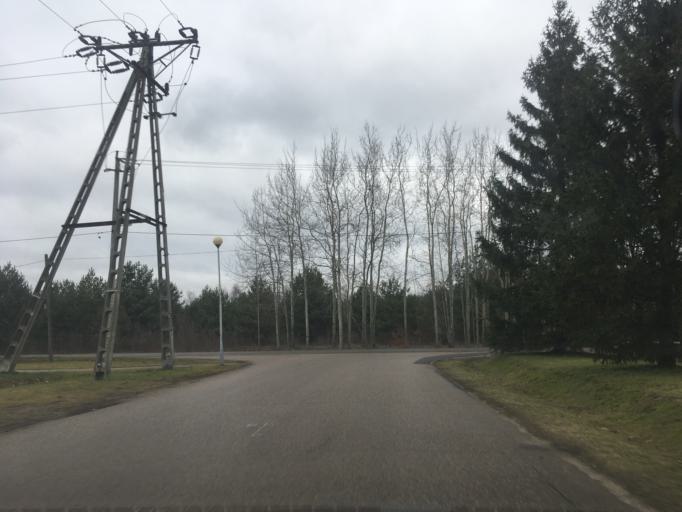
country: PL
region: Masovian Voivodeship
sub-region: Powiat piaseczynski
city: Lesznowola
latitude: 52.0604
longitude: 20.9077
